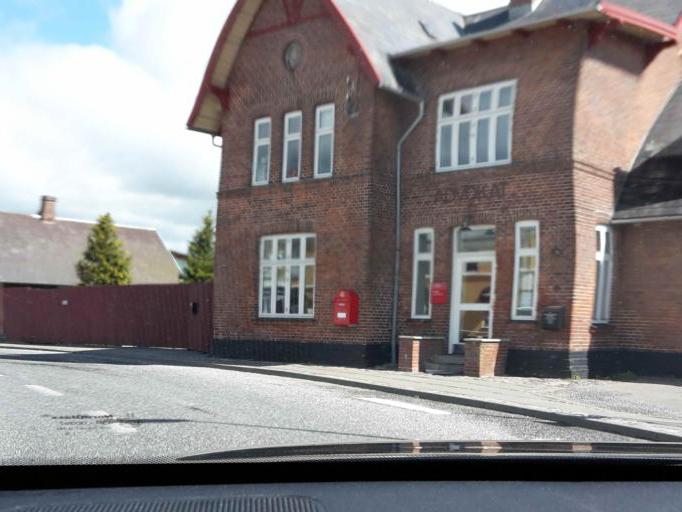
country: DK
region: Central Jutland
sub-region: Norddjurs Kommune
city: Auning
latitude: 56.4290
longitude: 10.3774
